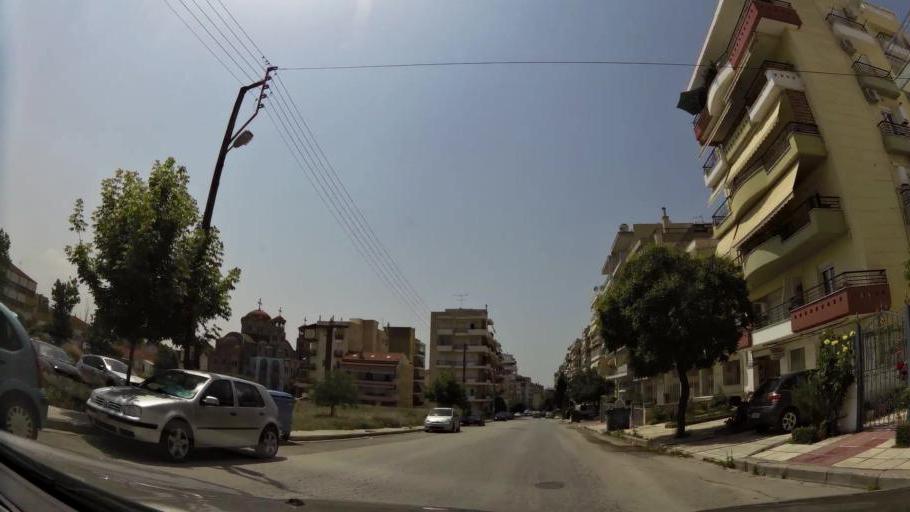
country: GR
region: Central Macedonia
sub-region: Nomos Thessalonikis
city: Evosmos
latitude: 40.6759
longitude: 22.9085
